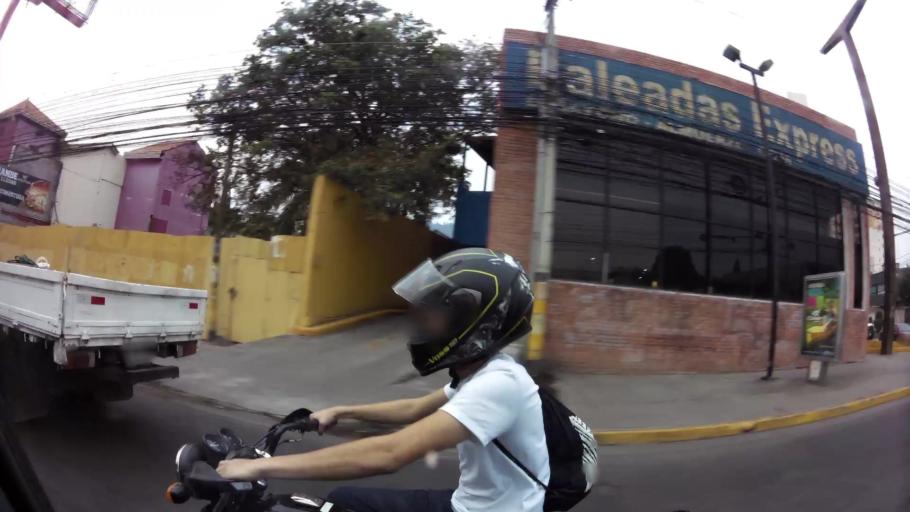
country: HN
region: Francisco Morazan
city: Tegucigalpa
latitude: 14.0999
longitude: -87.1925
